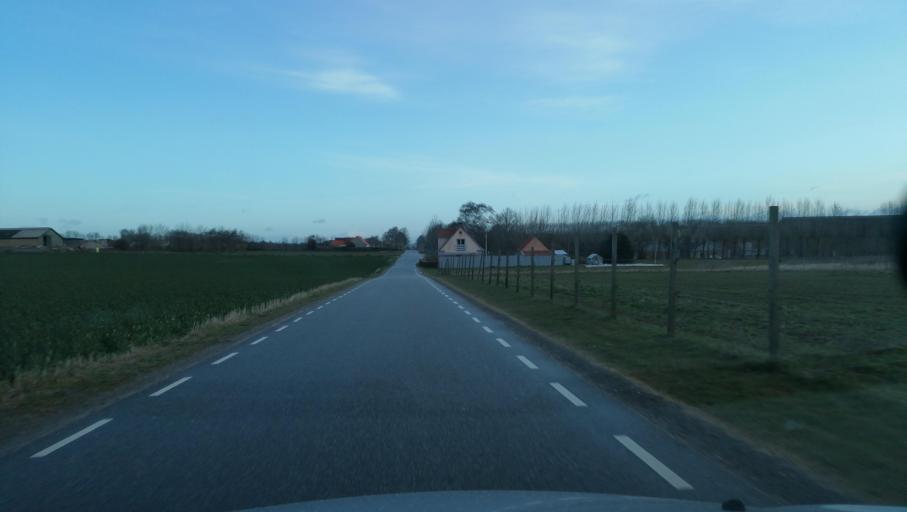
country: DK
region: Zealand
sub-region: Odsherred Kommune
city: Horve
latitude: 55.7559
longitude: 11.4403
